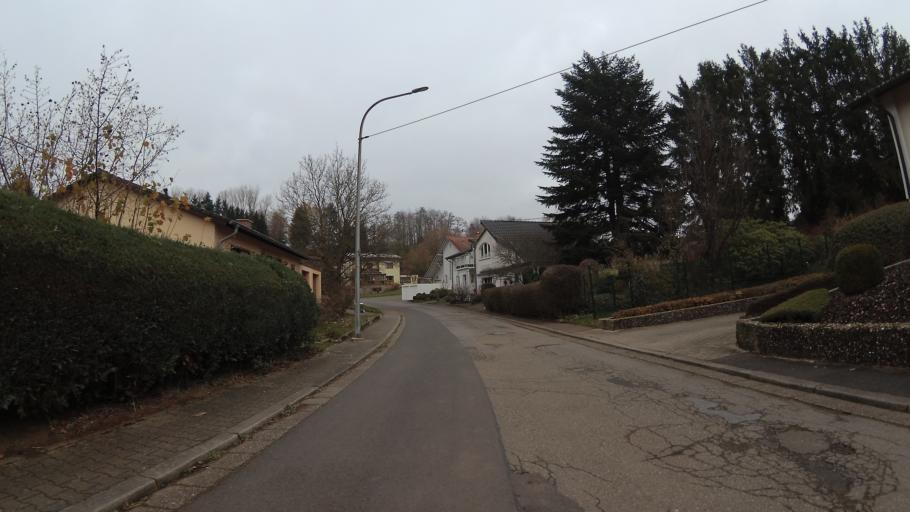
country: DE
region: Saarland
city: Schiffweiler
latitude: 49.3742
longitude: 7.1153
